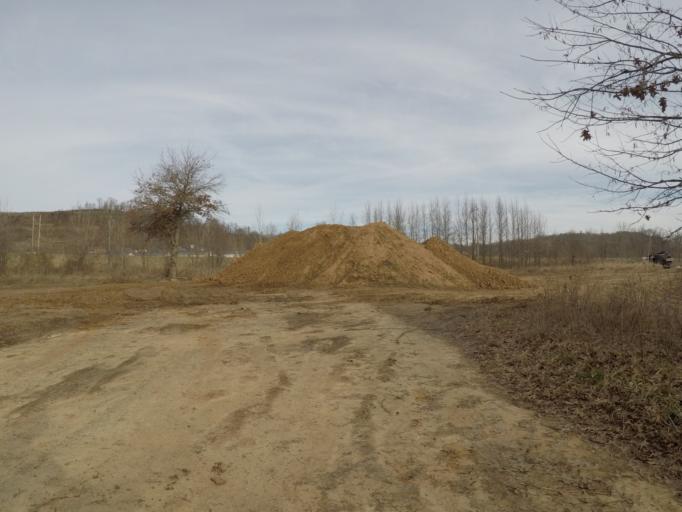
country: US
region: West Virginia
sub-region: Cabell County
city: Huntington
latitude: 38.4436
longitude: -82.3816
